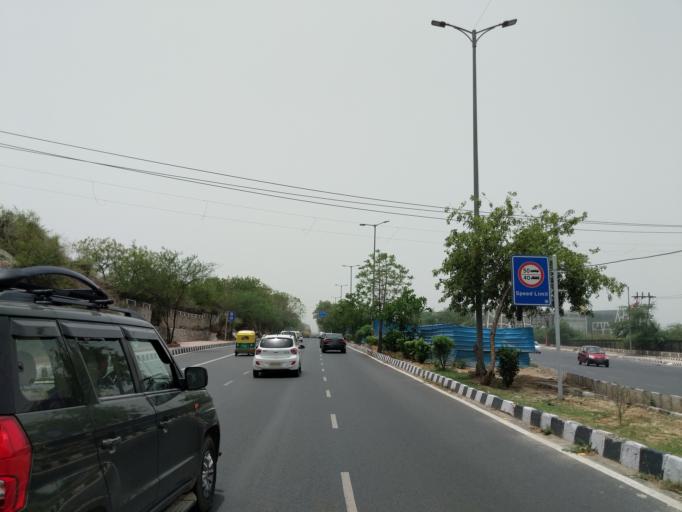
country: IN
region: NCT
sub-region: Central Delhi
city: Karol Bagh
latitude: 28.5469
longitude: 77.1616
